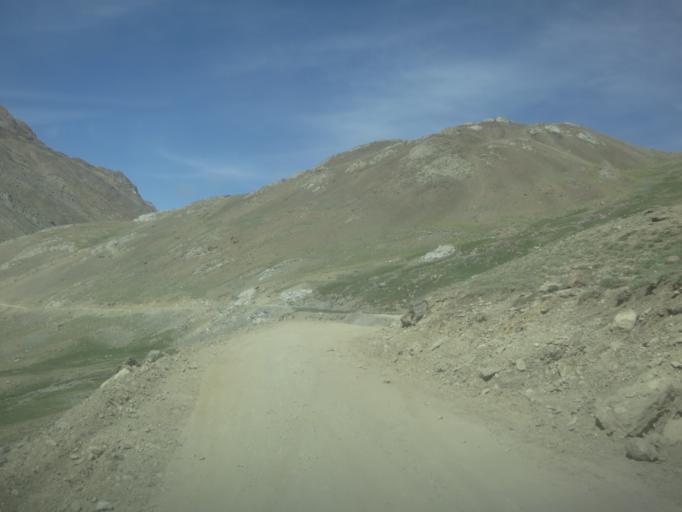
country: IN
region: Himachal Pradesh
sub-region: Kulu
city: Manali
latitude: 32.4163
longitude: 77.6504
